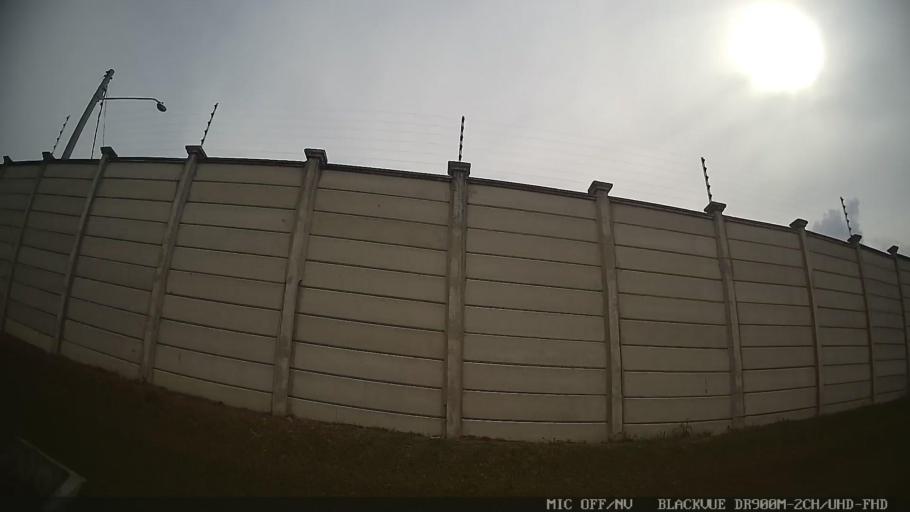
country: BR
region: Sao Paulo
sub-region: Indaiatuba
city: Indaiatuba
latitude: -23.0934
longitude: -47.2531
